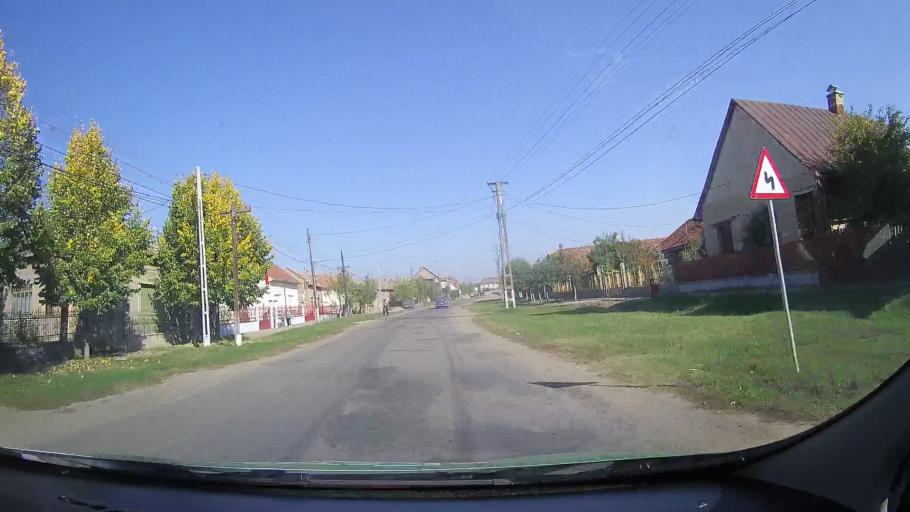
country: RO
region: Satu Mare
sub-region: Comuna Sanislau
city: Sanislau
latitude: 47.6385
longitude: 22.3240
